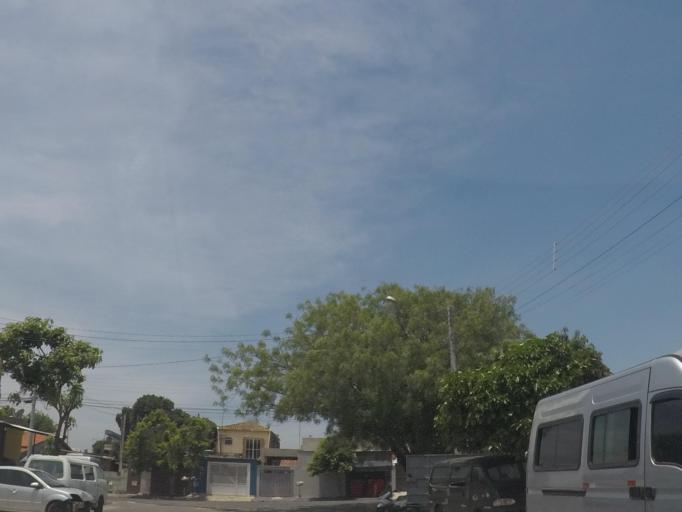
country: BR
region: Sao Paulo
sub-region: Hortolandia
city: Hortolandia
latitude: -22.8557
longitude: -47.1793
